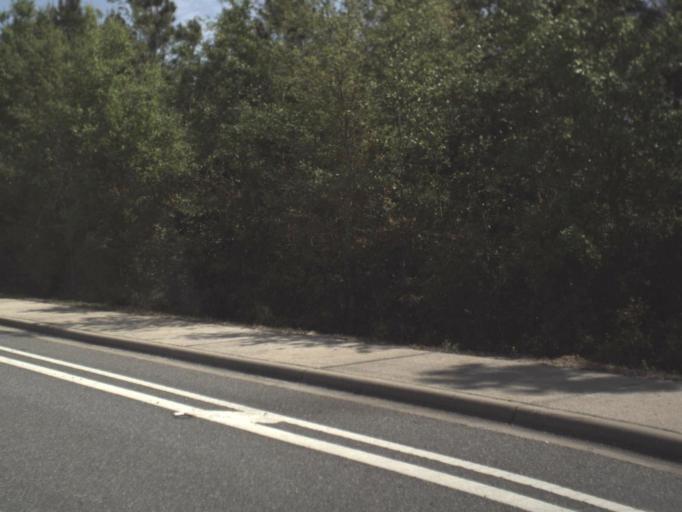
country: US
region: Florida
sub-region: Santa Rosa County
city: Navarre
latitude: 30.4030
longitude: -86.8712
